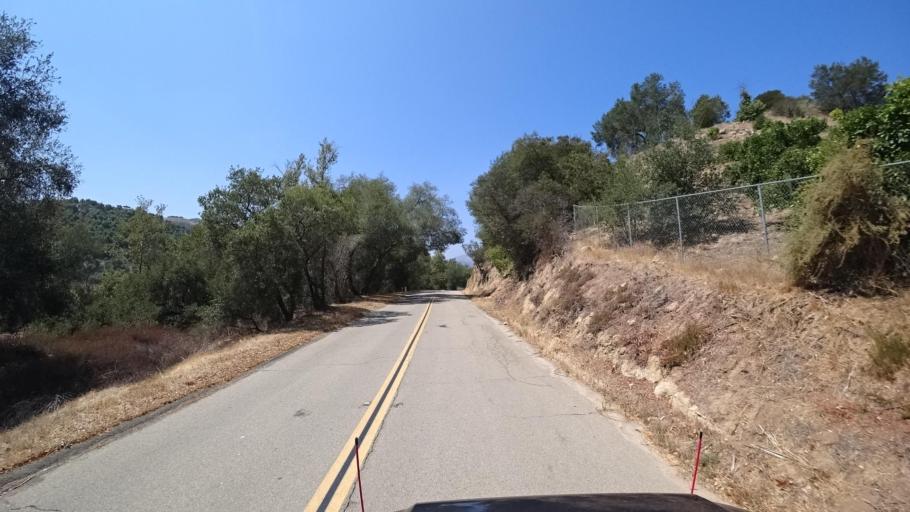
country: US
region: California
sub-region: San Diego County
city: Fallbrook
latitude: 33.4548
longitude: -117.3026
